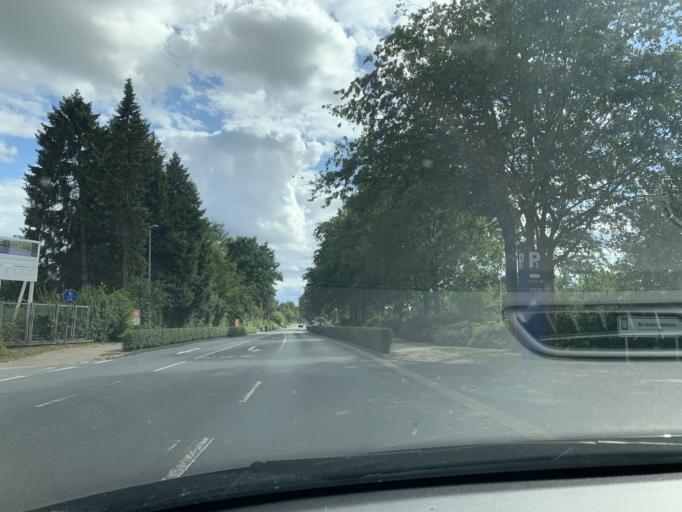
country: DE
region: Lower Saxony
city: Bad Zwischenahn
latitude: 53.2002
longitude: 7.9945
